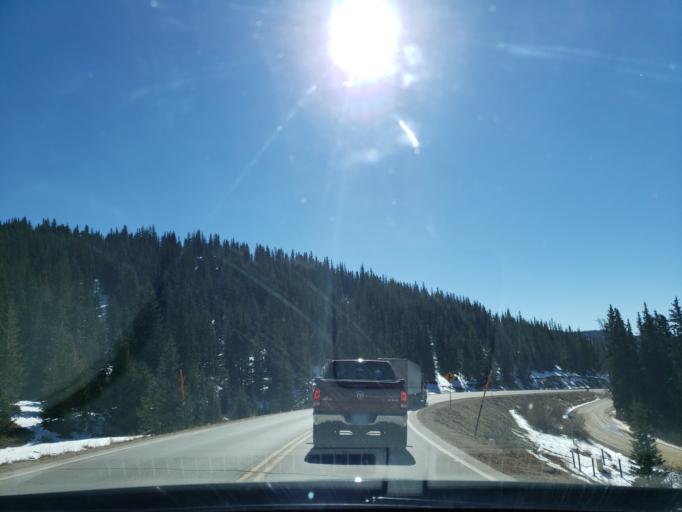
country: US
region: Colorado
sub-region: Summit County
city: Breckenridge
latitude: 39.3508
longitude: -106.0552
